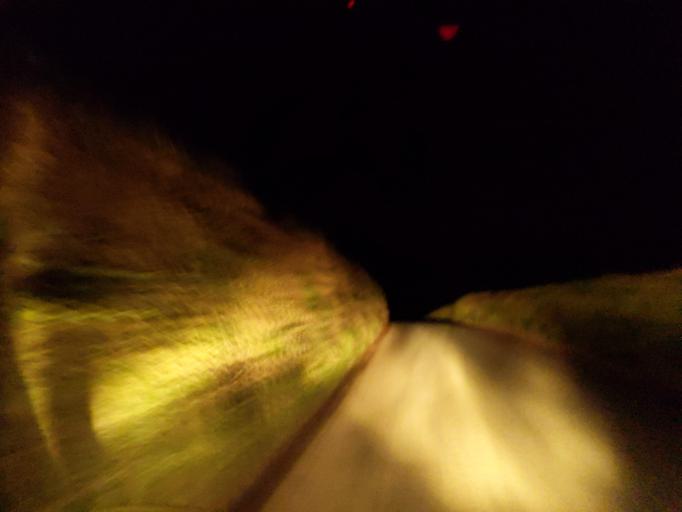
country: GB
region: England
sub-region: Cornwall
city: Saltash
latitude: 50.3602
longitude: -4.2855
